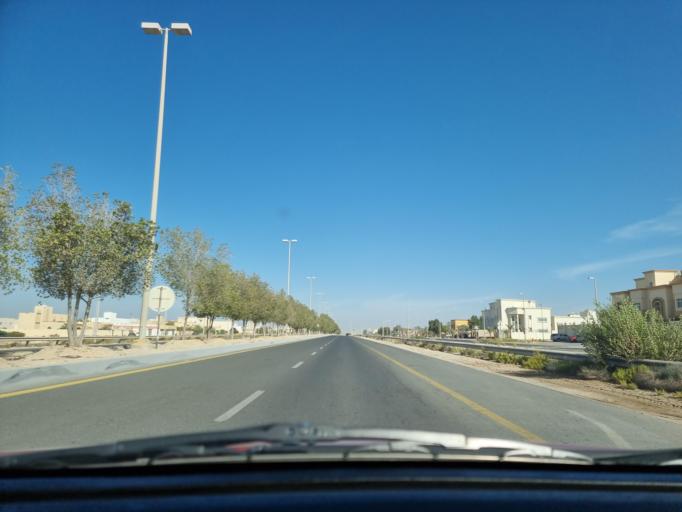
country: AE
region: Abu Dhabi
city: Abu Dhabi
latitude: 24.3860
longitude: 54.6955
